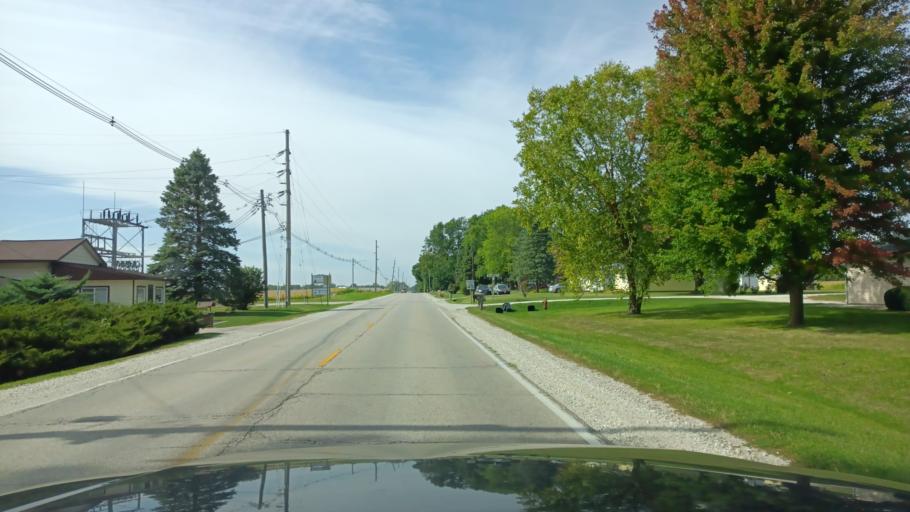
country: US
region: Illinois
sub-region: Knox County
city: Knoxville
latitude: 40.9126
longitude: -90.2980
